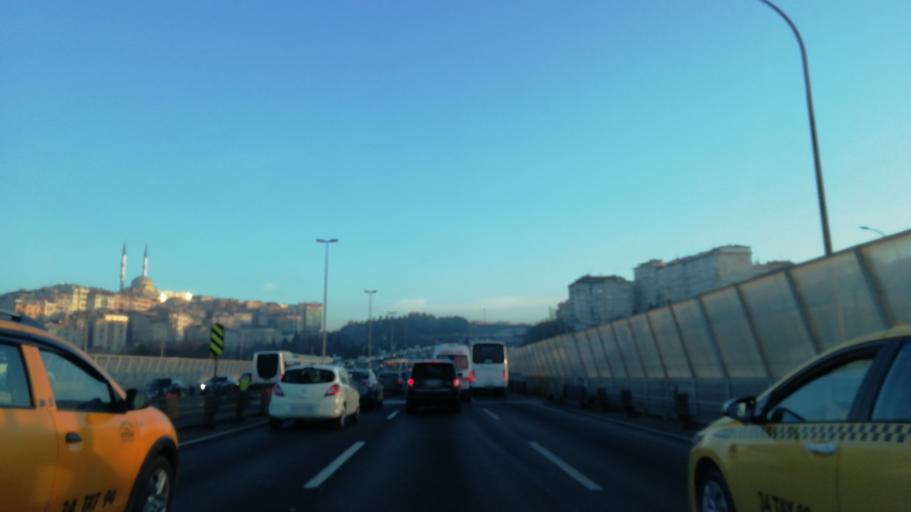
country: TR
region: Istanbul
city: Istanbul
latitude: 41.0460
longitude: 28.9439
